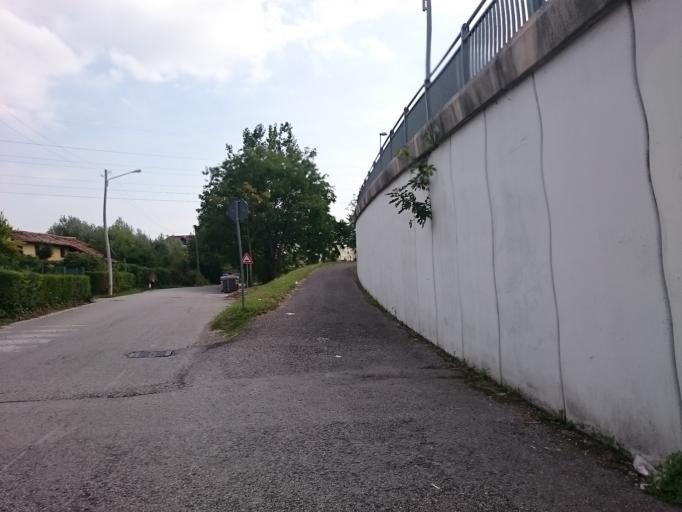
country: IT
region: Veneto
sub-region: Provincia di Padova
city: Padova
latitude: 45.4180
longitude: 11.9097
